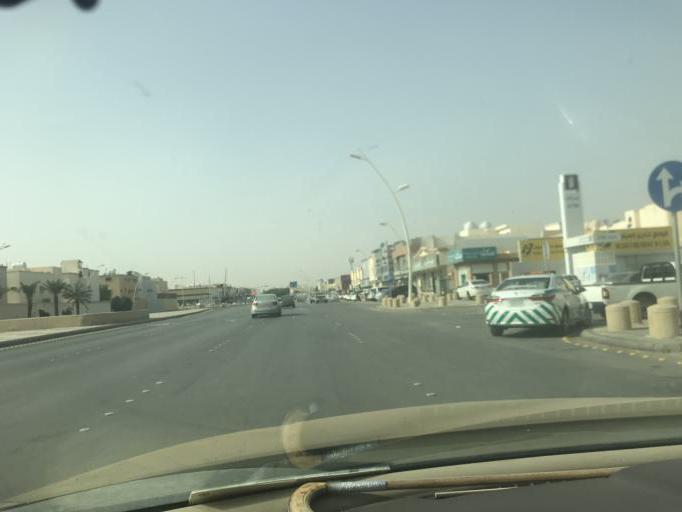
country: SA
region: Ar Riyad
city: Riyadh
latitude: 24.6808
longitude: 46.7992
